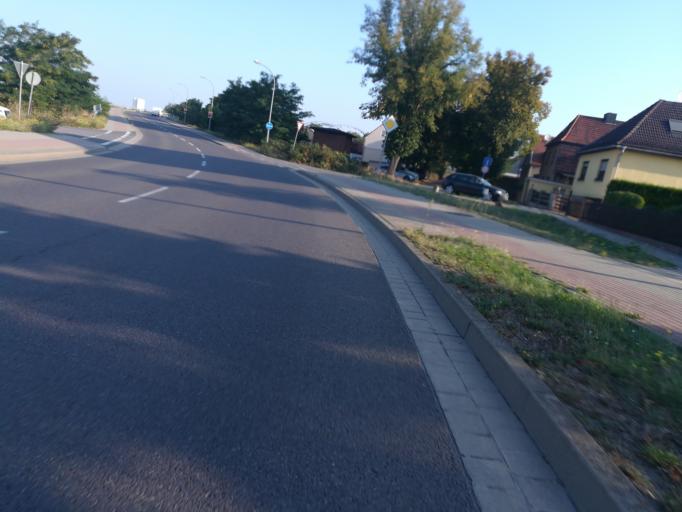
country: DE
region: Saxony-Anhalt
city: Haldensleben I
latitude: 52.2723
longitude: 11.4222
